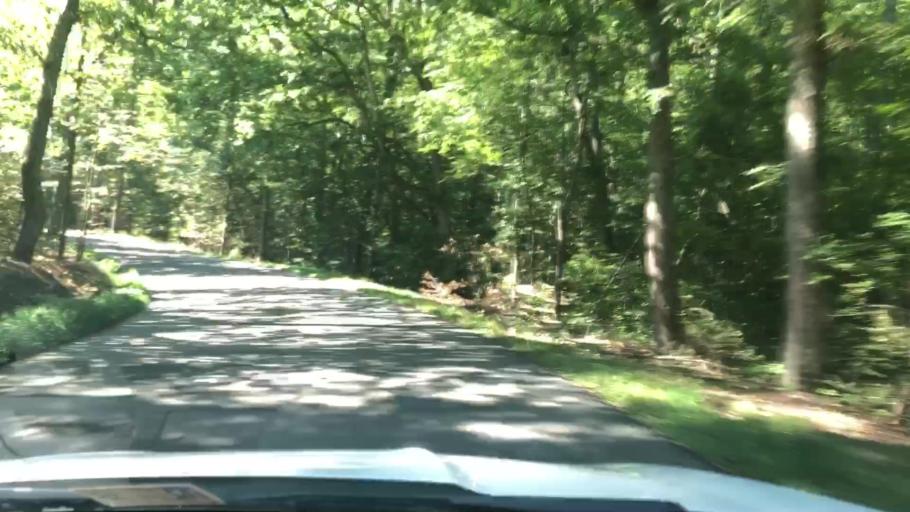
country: US
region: Virginia
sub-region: New Kent County
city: New Kent
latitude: 37.4872
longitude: -76.9353
